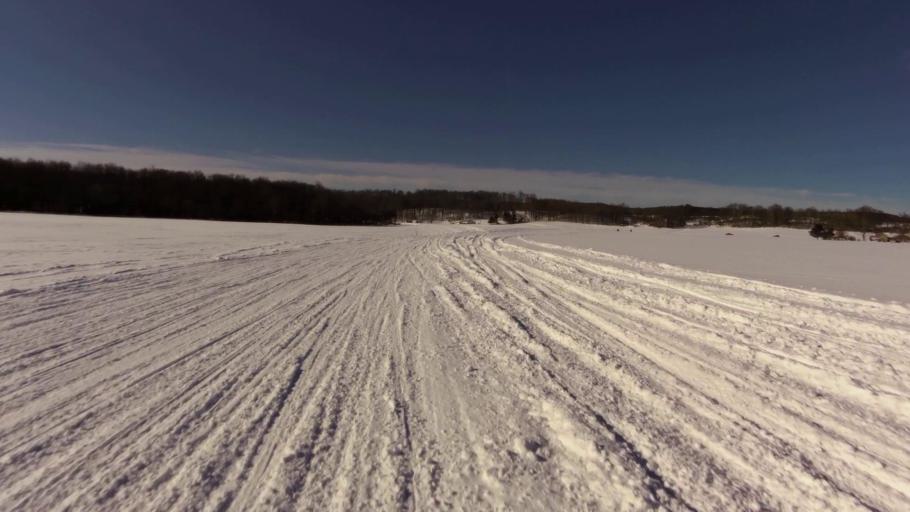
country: US
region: New York
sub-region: Cattaraugus County
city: Franklinville
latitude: 42.3937
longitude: -78.4747
